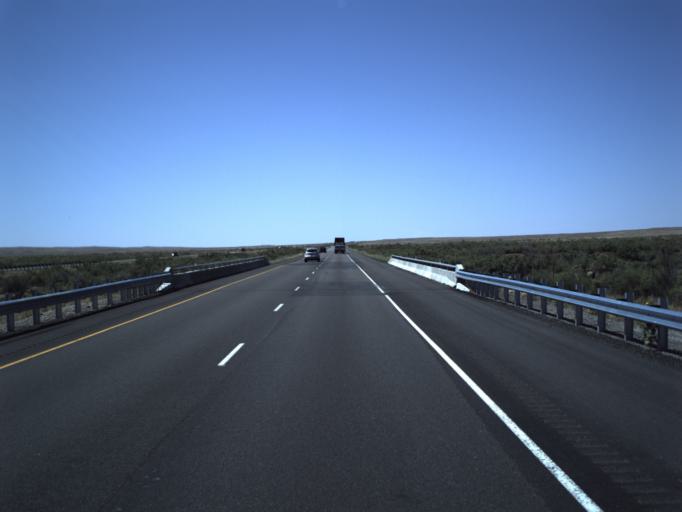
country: US
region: Colorado
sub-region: Mesa County
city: Loma
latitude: 39.0819
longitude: -109.2254
